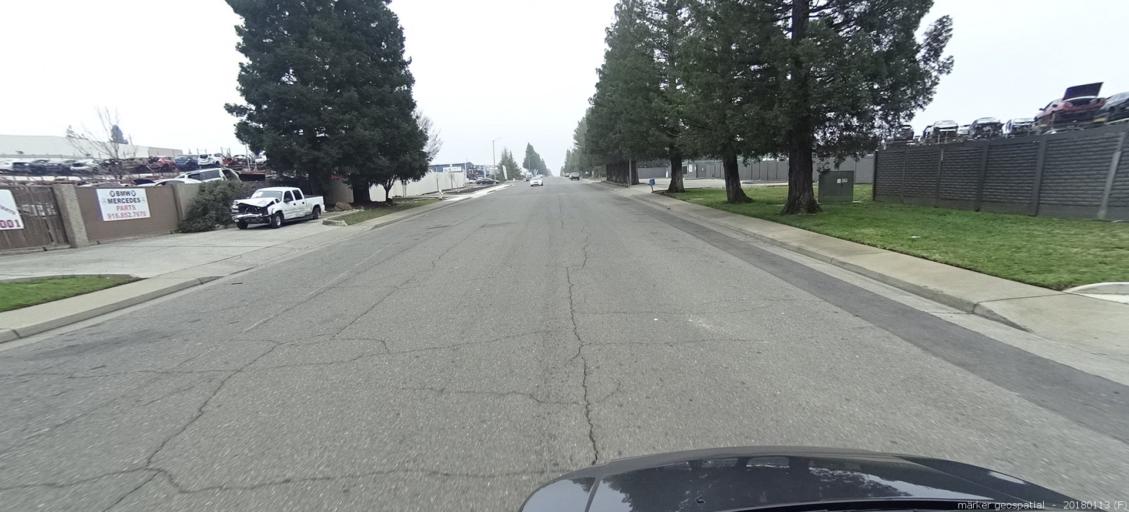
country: US
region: California
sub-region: Sacramento County
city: Rancho Cordova
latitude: 38.5767
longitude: -121.2622
